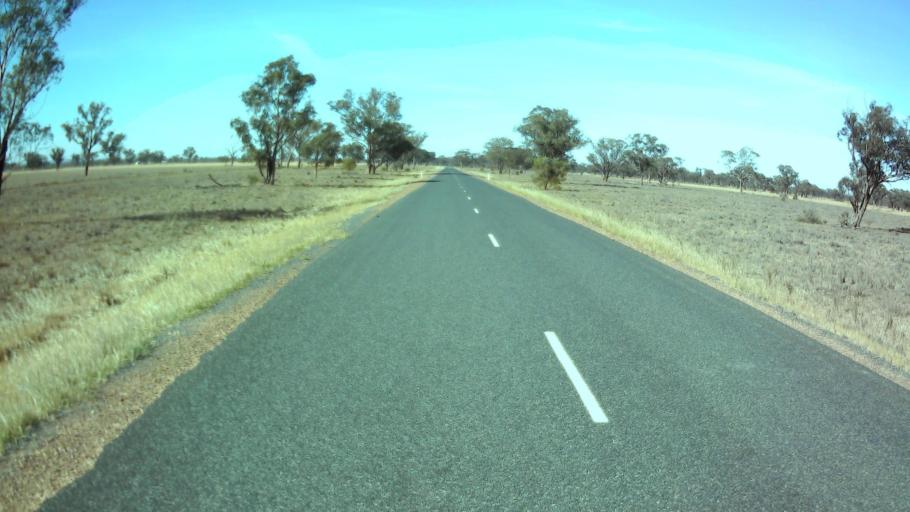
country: AU
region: New South Wales
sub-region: Weddin
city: Grenfell
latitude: -34.0740
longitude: 147.9009
